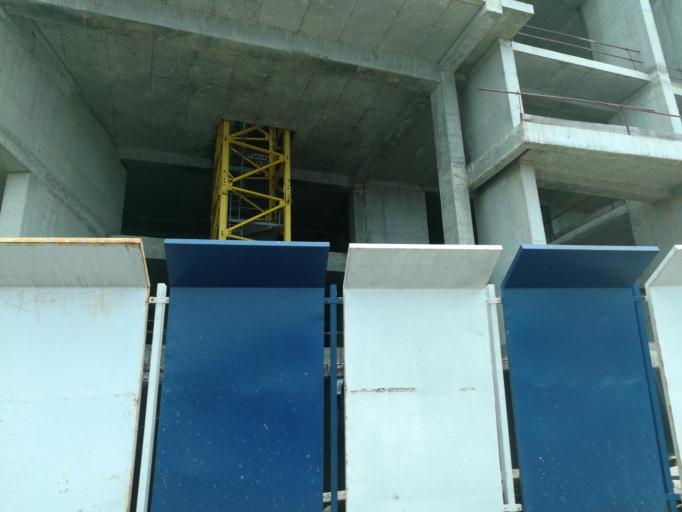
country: NG
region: Lagos
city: Lagos
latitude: 6.4020
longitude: 3.4063
